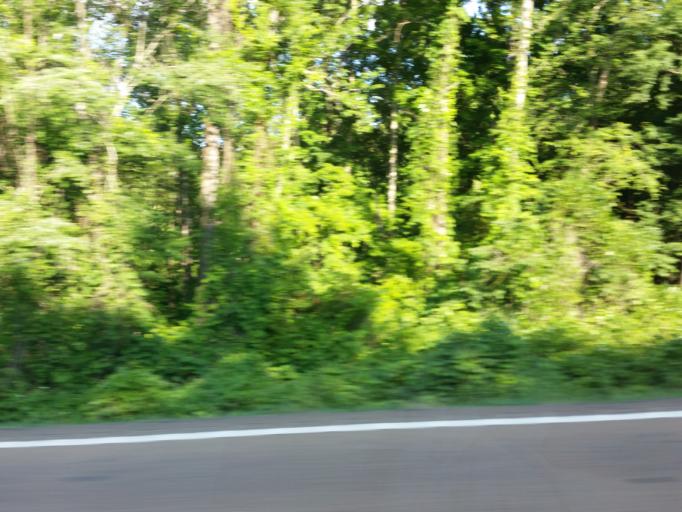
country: US
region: Mississippi
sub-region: Calhoun County
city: Calhoun City
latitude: 33.8031
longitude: -89.3538
